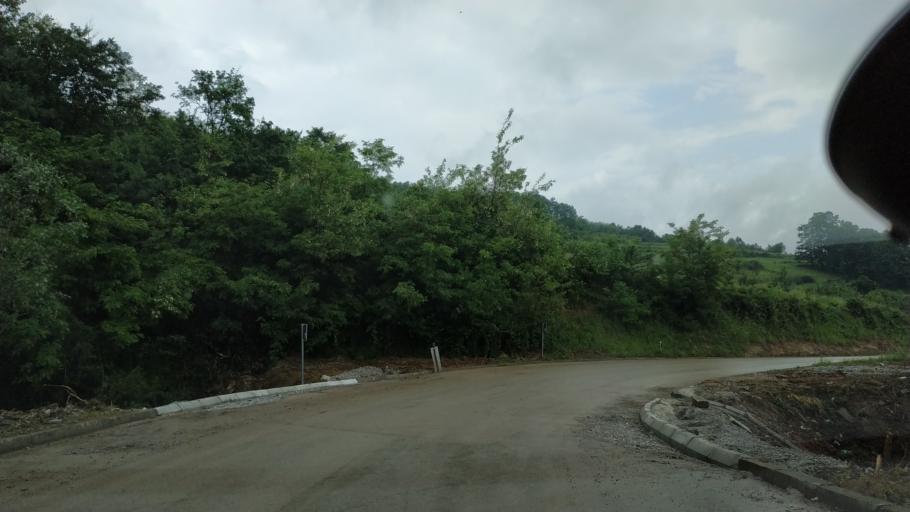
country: RS
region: Central Serbia
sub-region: Toplicki Okrug
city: Prokuplje
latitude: 43.4092
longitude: 21.5515
